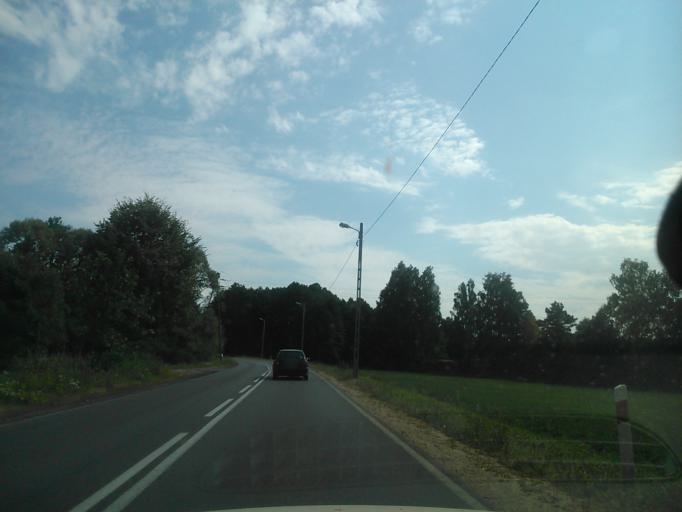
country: PL
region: Warmian-Masurian Voivodeship
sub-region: Powiat dzialdowski
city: Ilowo -Osada
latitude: 53.1488
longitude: 20.3322
